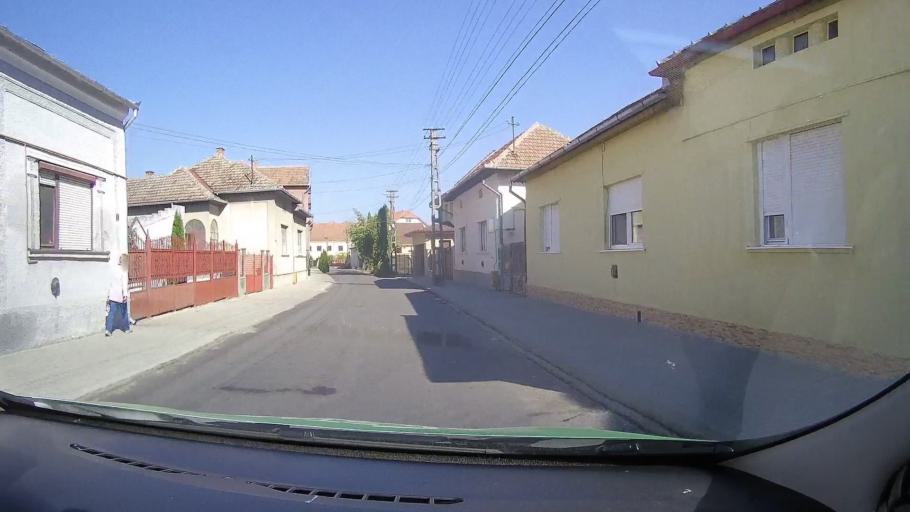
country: RO
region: Satu Mare
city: Carei
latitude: 47.6862
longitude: 22.4660
